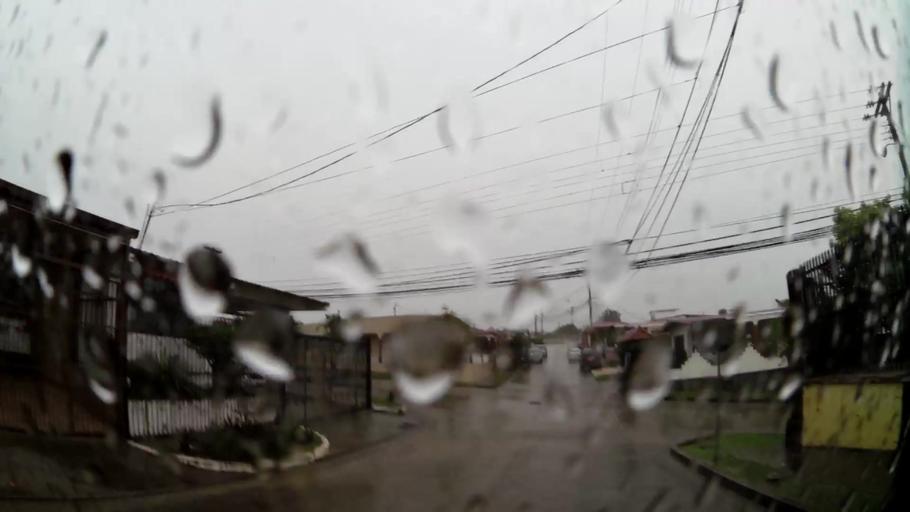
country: PA
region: Panama
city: San Miguelito
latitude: 9.0491
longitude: -79.4665
